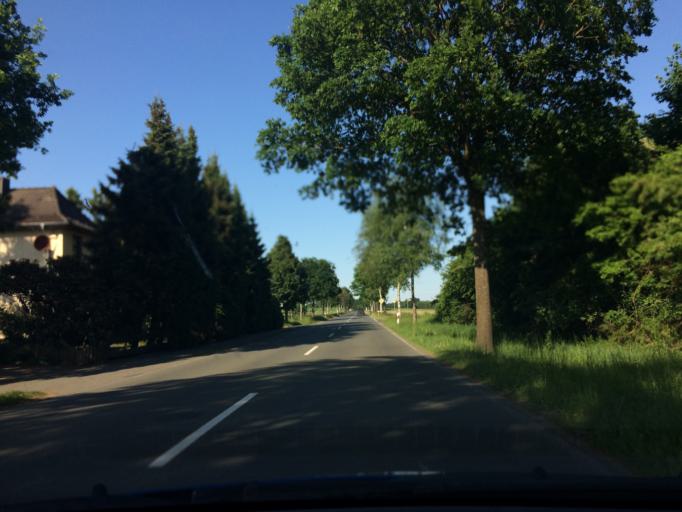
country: DE
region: Lower Saxony
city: Soltau
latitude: 53.0259
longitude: 9.9109
